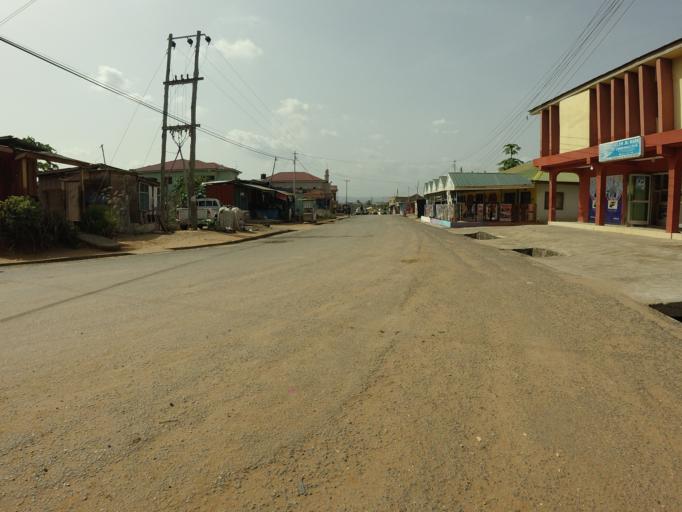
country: GH
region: Greater Accra
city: Dome
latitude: 5.6103
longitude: -0.2397
